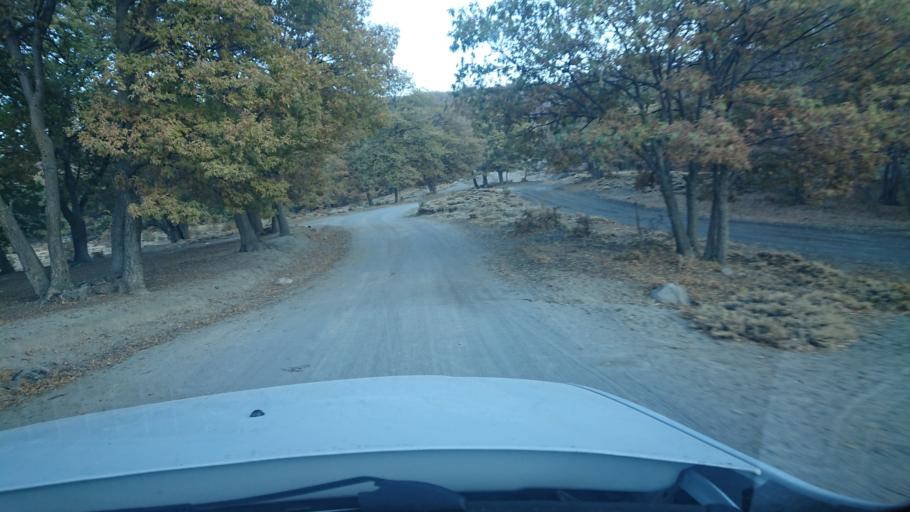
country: TR
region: Aksaray
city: Taspinar
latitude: 38.1663
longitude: 34.2044
